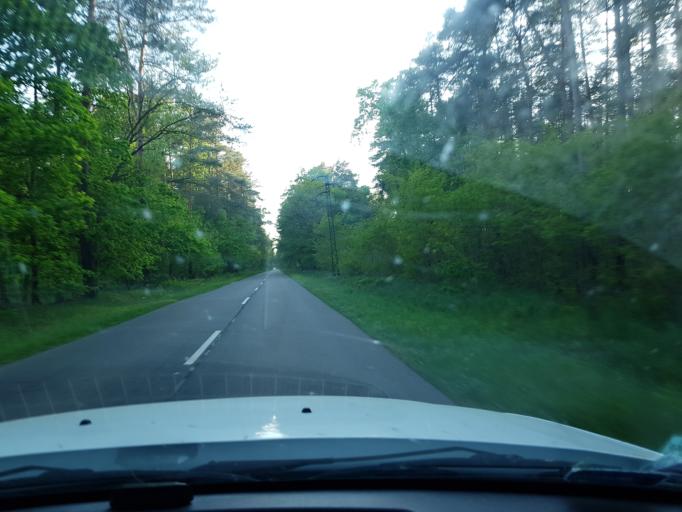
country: PL
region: West Pomeranian Voivodeship
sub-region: Powiat goleniowski
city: Mosty
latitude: 53.4460
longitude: 14.9256
